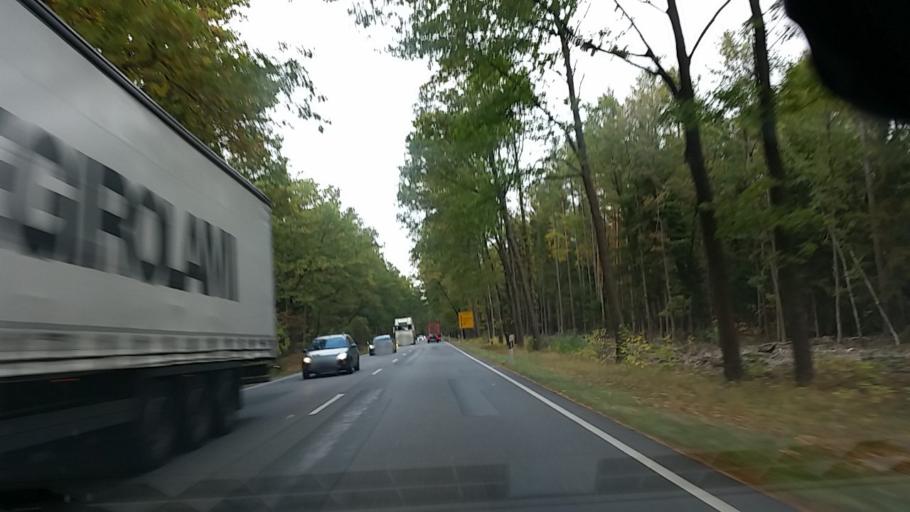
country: DE
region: Lower Saxony
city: Sprakensehl
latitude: 52.7831
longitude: 10.4914
